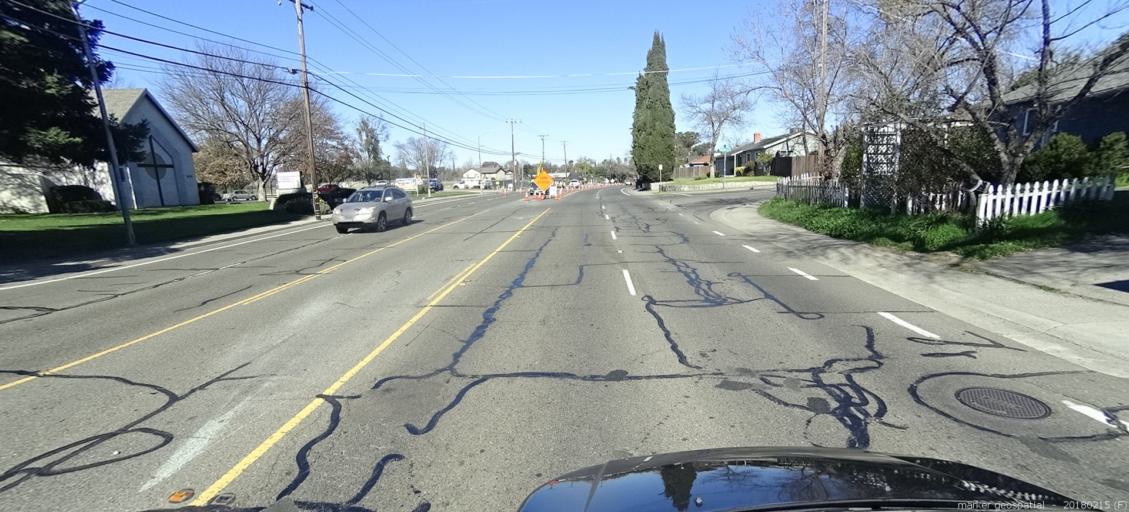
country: US
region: California
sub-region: Sacramento County
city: Antelope
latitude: 38.6722
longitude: -121.3092
